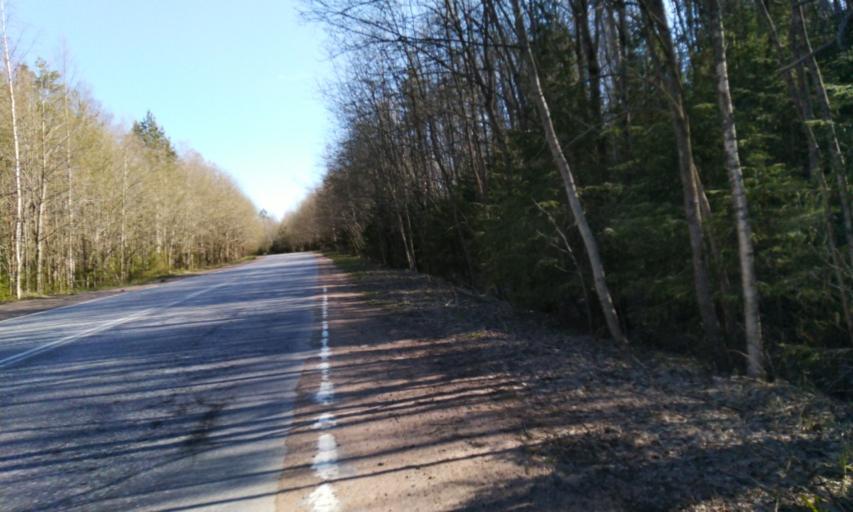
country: RU
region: Leningrad
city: Garbolovo
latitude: 60.3848
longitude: 30.4720
